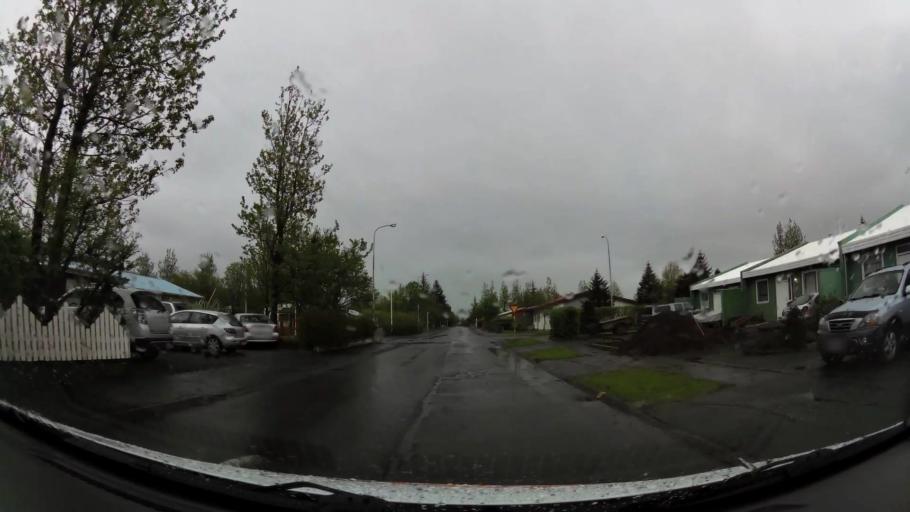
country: IS
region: South
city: Hveragerdi
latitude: 64.0021
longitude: -21.1965
